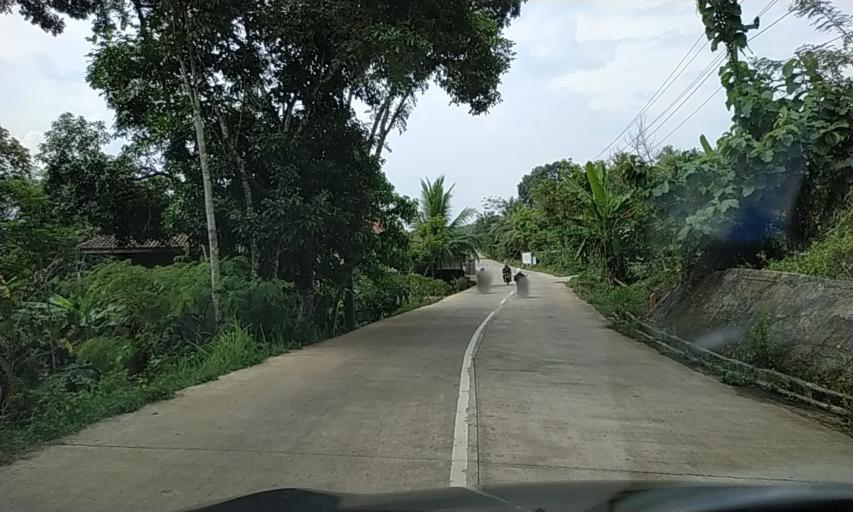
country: ID
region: Central Java
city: Winangun
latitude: -7.3669
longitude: 108.6991
